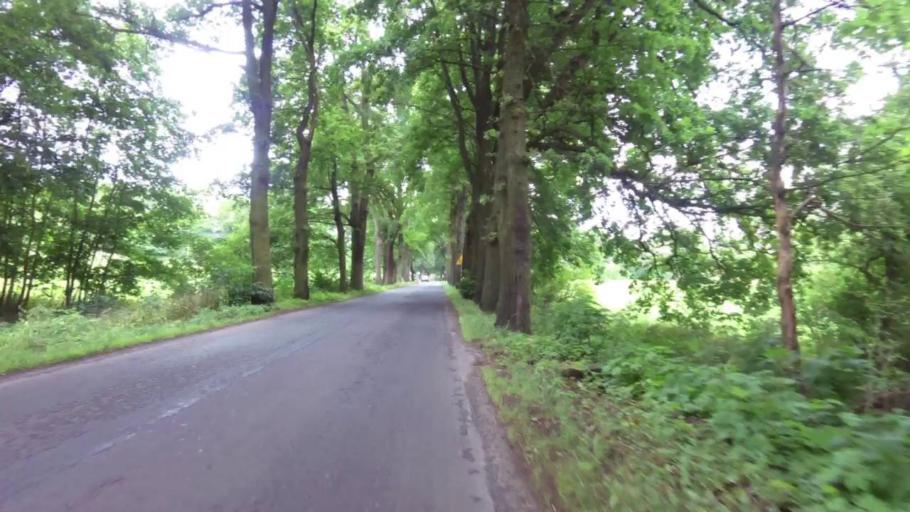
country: PL
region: West Pomeranian Voivodeship
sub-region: Powiat gryfinski
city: Moryn
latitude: 52.8711
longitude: 14.3792
